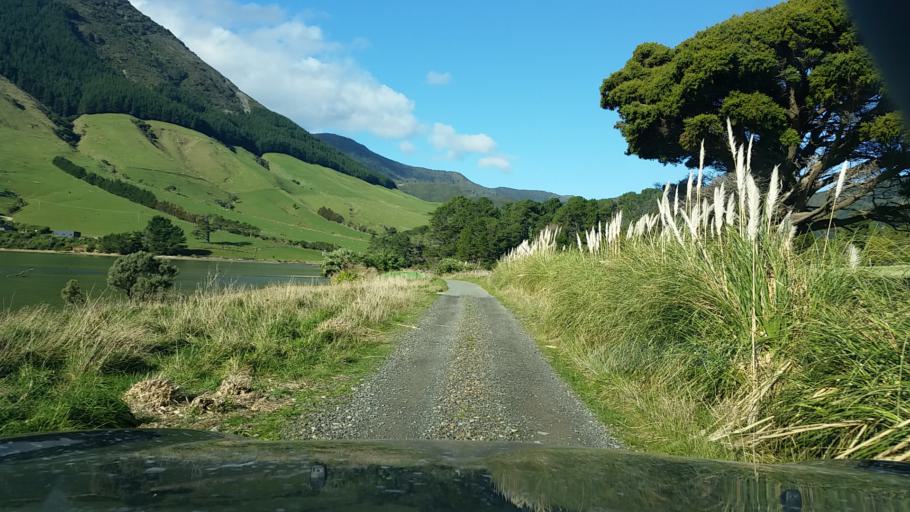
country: NZ
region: Marlborough
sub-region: Marlborough District
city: Picton
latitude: -41.1110
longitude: 174.0332
